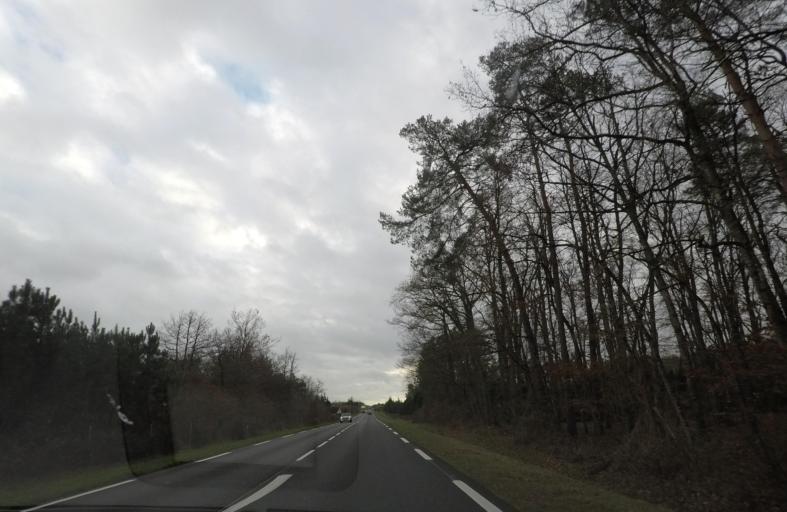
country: FR
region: Centre
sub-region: Departement du Loir-et-Cher
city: Soings-en-Sologne
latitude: 47.4677
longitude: 1.5110
